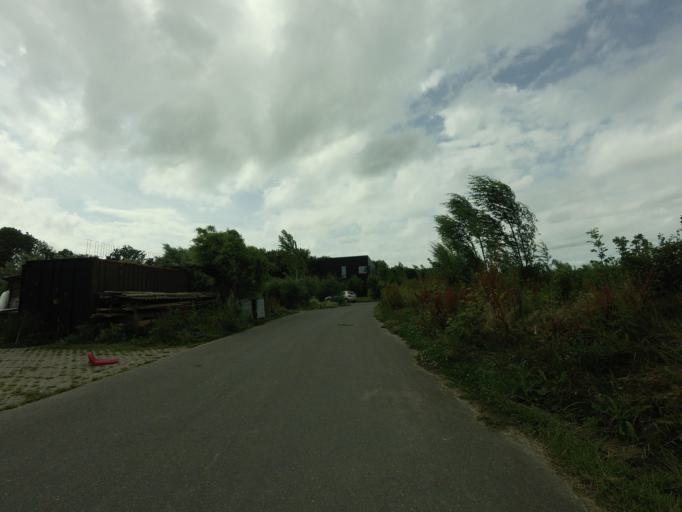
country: NL
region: North Holland
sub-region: Gemeente Huizen
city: Huizen
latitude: 52.3310
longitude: 5.3153
